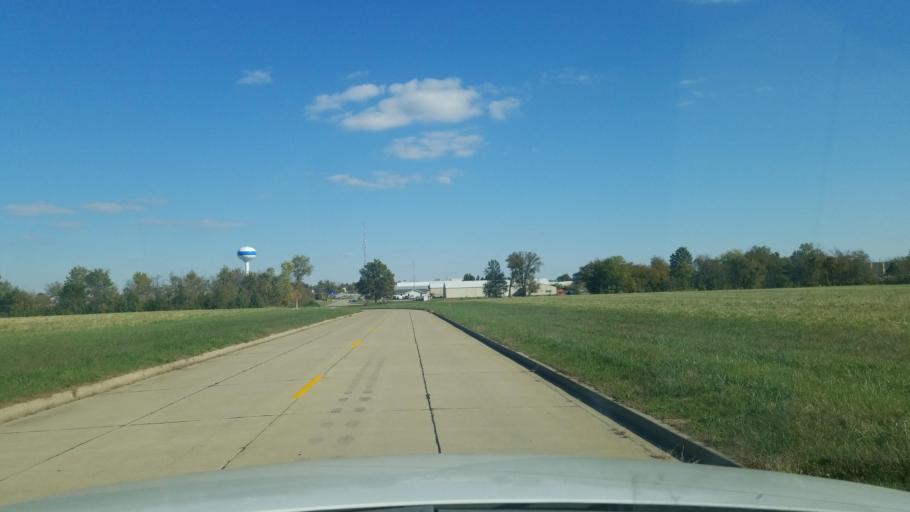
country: US
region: Illinois
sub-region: Williamson County
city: Energy
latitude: 37.7394
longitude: -88.9916
